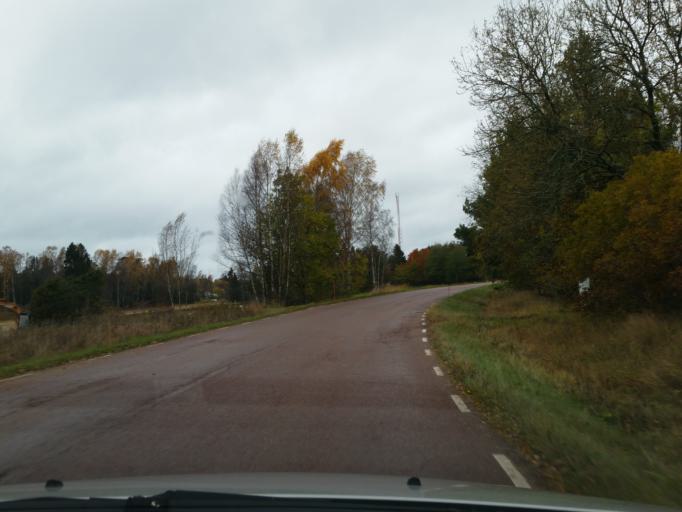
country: AX
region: Alands landsbygd
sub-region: Lumparland
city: Lumparland
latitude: 60.1122
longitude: 20.2642
